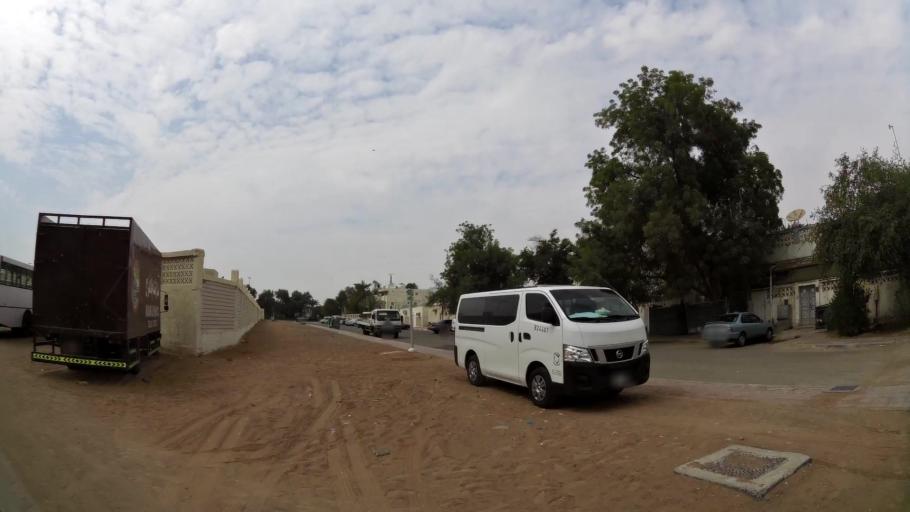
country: OM
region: Al Buraimi
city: Al Buraymi
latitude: 24.2179
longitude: 55.7878
